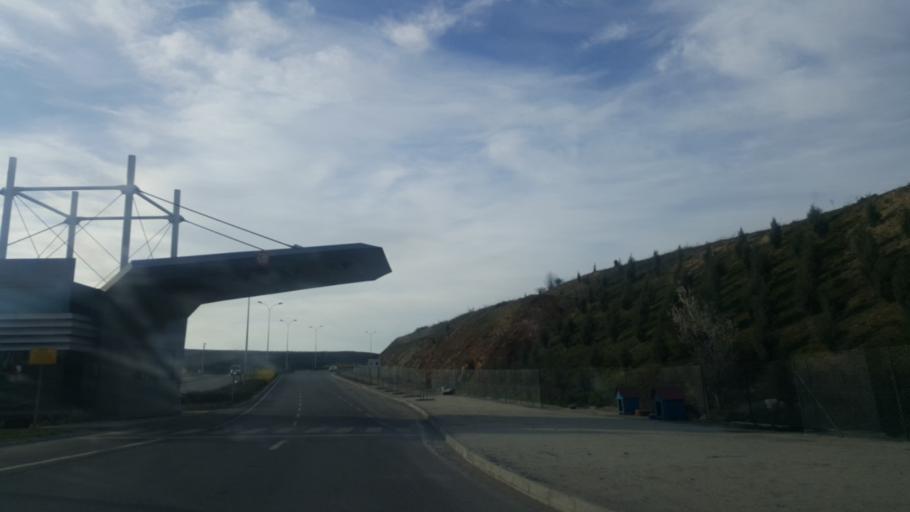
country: TR
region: Kocaeli
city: Tavsanli
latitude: 40.8276
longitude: 29.5617
